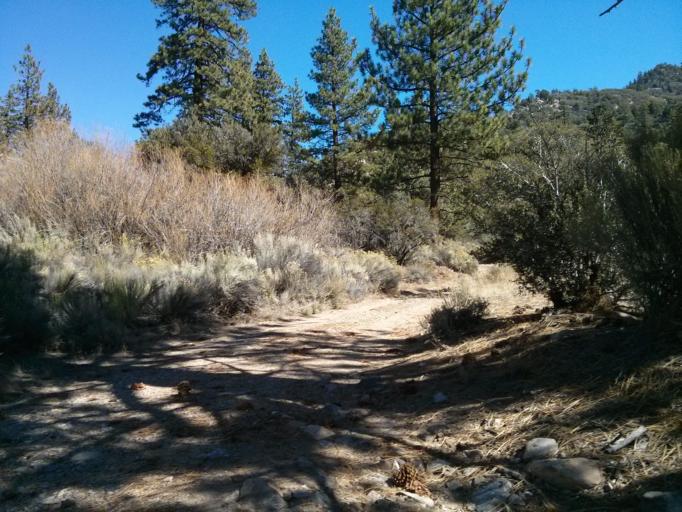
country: US
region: California
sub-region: San Bernardino County
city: Big Bear City
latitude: 34.1711
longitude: -116.7634
